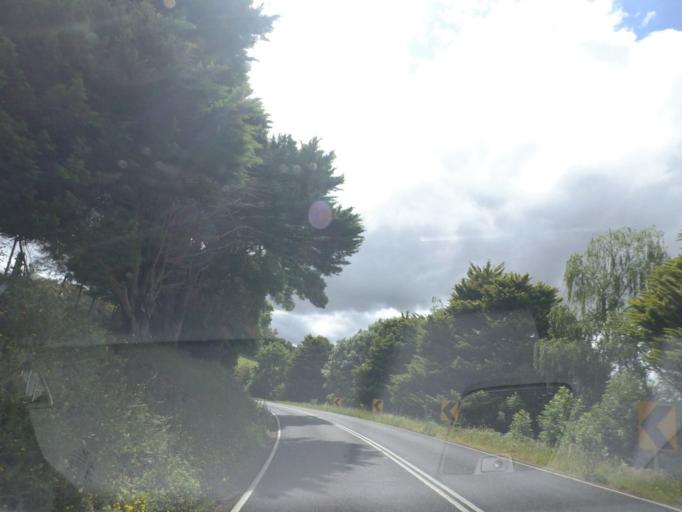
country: AU
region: Victoria
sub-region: Cardinia
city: Cockatoo
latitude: -37.9245
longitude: 145.4774
